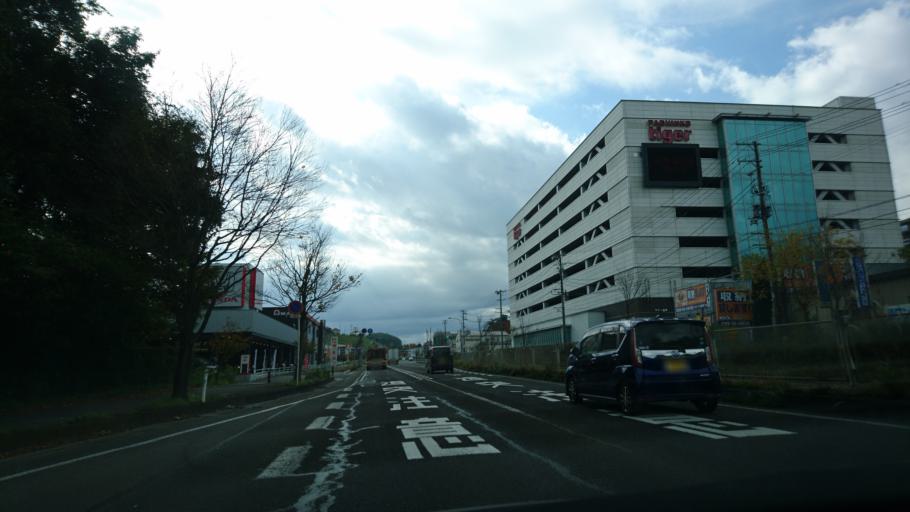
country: JP
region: Miyagi
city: Tomiya
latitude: 38.3716
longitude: 140.8741
